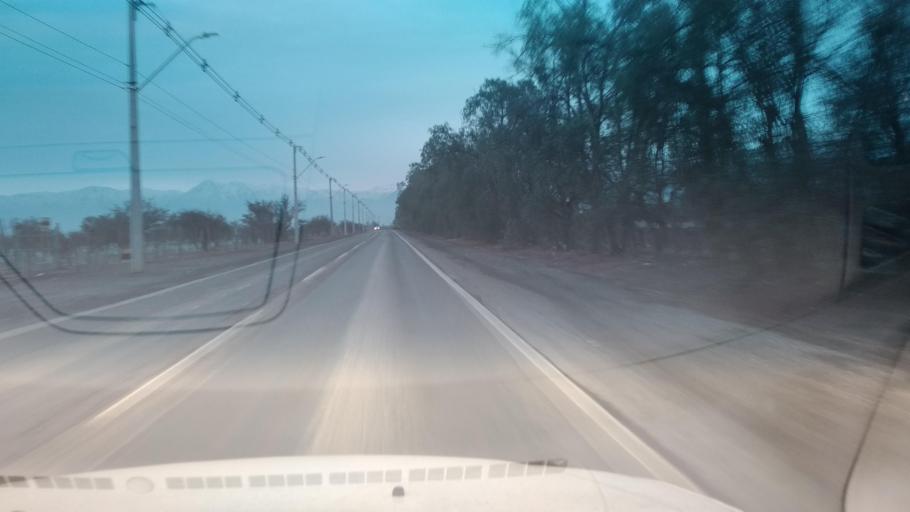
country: CL
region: Santiago Metropolitan
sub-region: Provincia de Chacabuco
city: Chicureo Abajo
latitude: -33.0969
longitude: -70.7520
